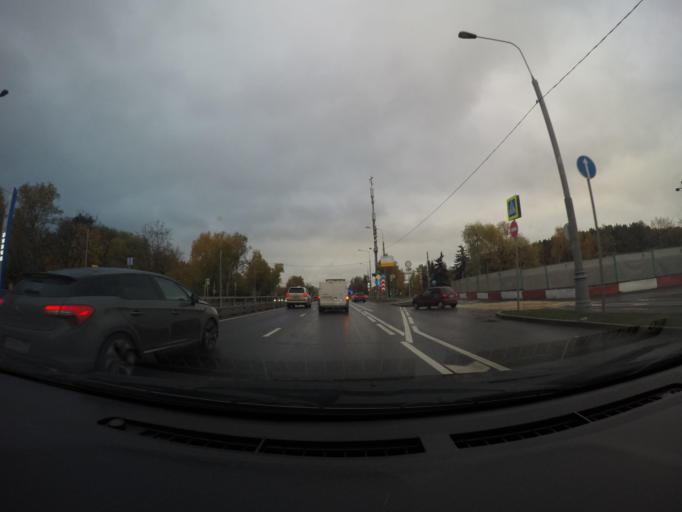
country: RU
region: Moskovskaya
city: Kastanayevo
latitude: 55.7267
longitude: 37.4952
